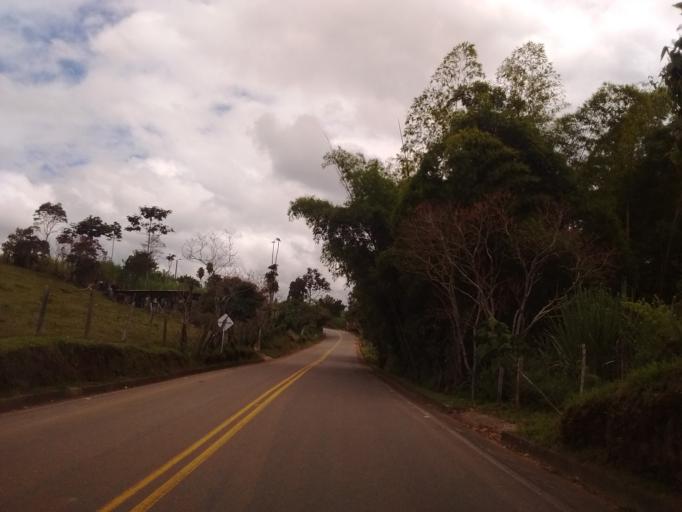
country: CO
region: Huila
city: Isnos
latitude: 1.9481
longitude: -76.2227
